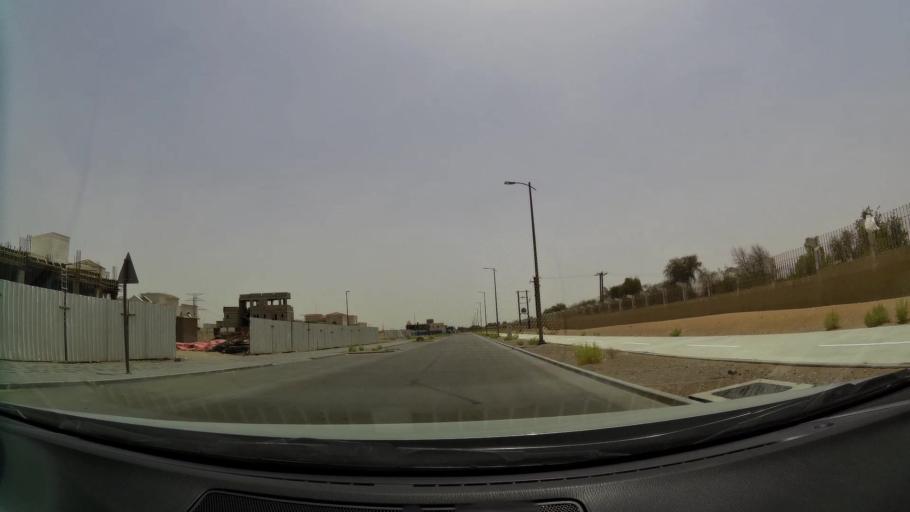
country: AE
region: Abu Dhabi
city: Al Ain
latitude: 24.1619
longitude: 55.6480
